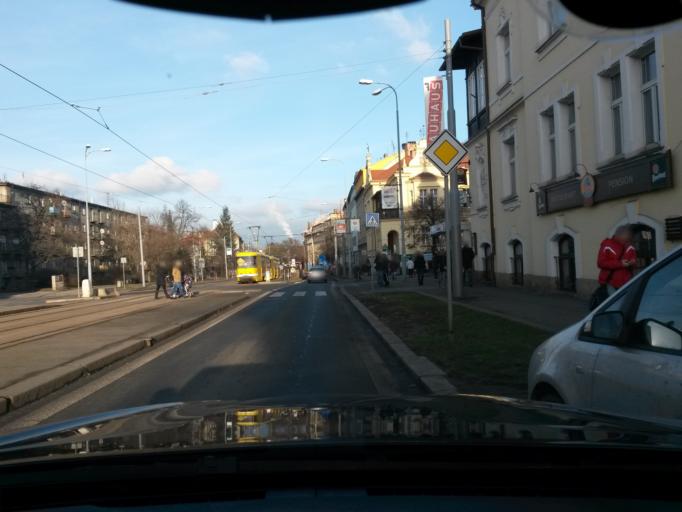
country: CZ
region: Plzensky
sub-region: Okres Plzen-Mesto
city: Pilsen
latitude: 49.7277
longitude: 13.3677
